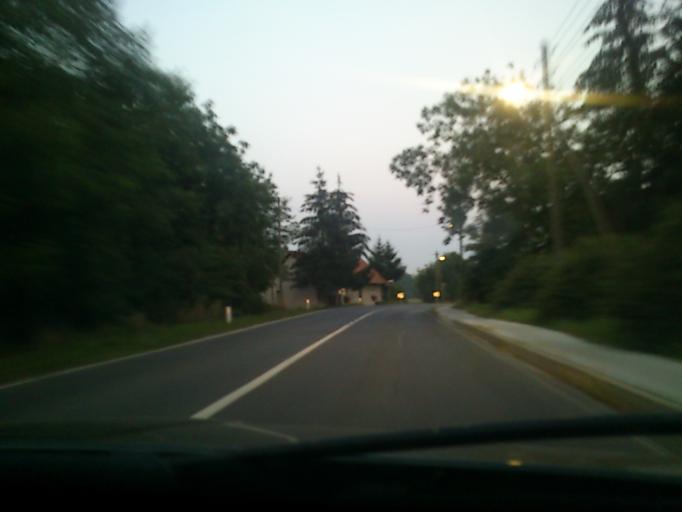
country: SI
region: Duplek
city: Spodnji Duplek
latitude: 46.4852
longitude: 15.7340
